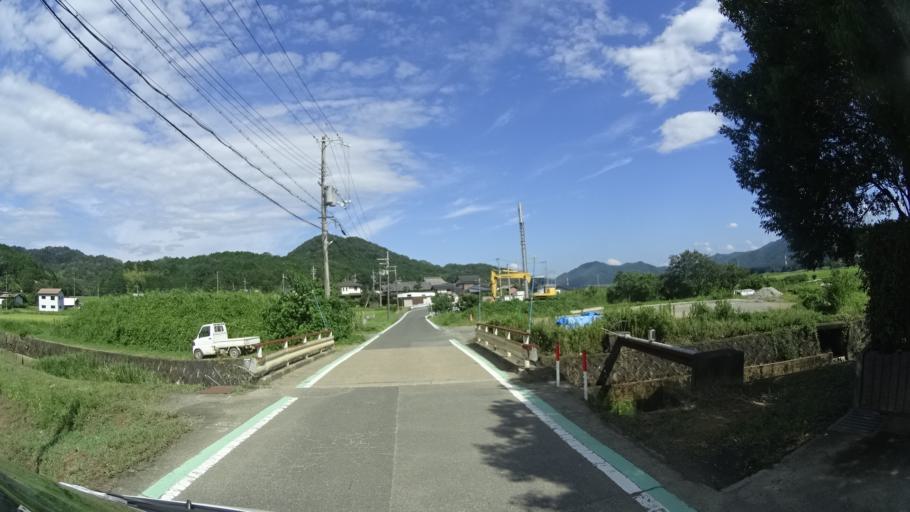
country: JP
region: Kyoto
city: Fukuchiyama
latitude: 35.3186
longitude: 135.1823
